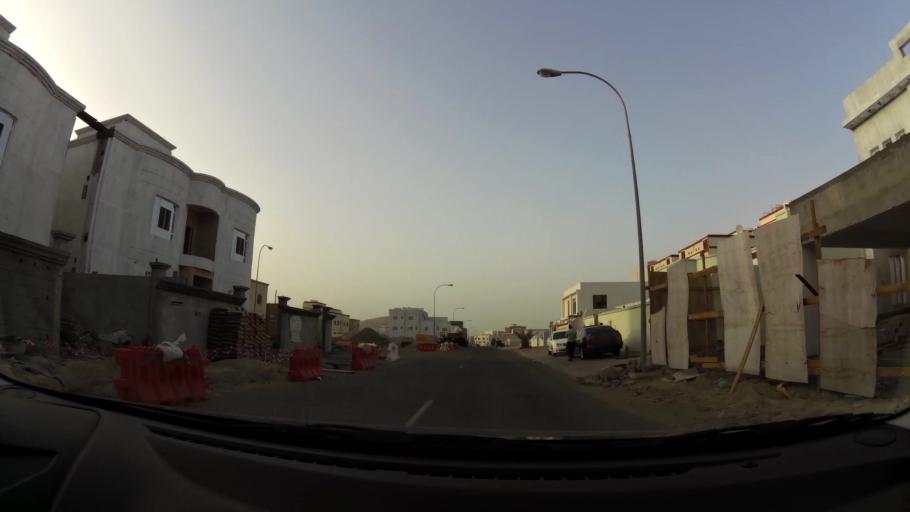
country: OM
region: Muhafazat Masqat
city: Bawshar
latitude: 23.4966
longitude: 58.3191
